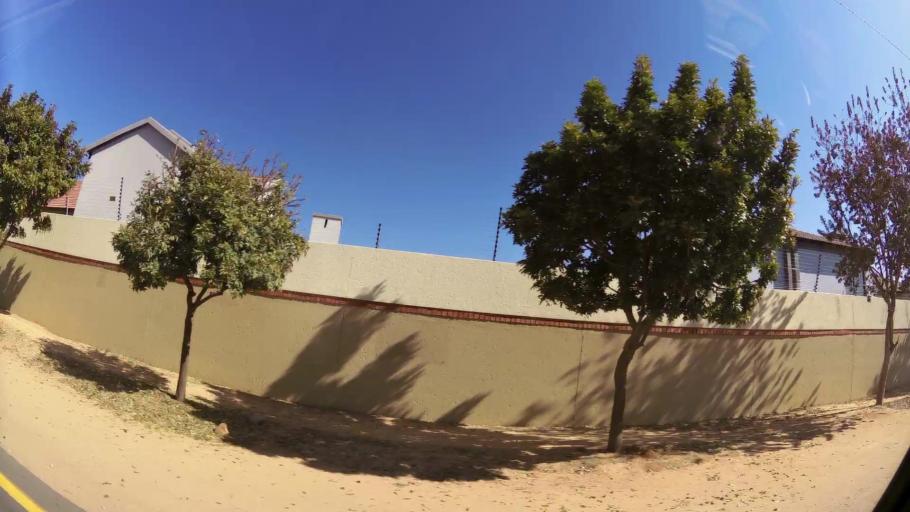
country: ZA
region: Gauteng
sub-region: City of Johannesburg Metropolitan Municipality
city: Midrand
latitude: -25.9641
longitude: 28.1015
